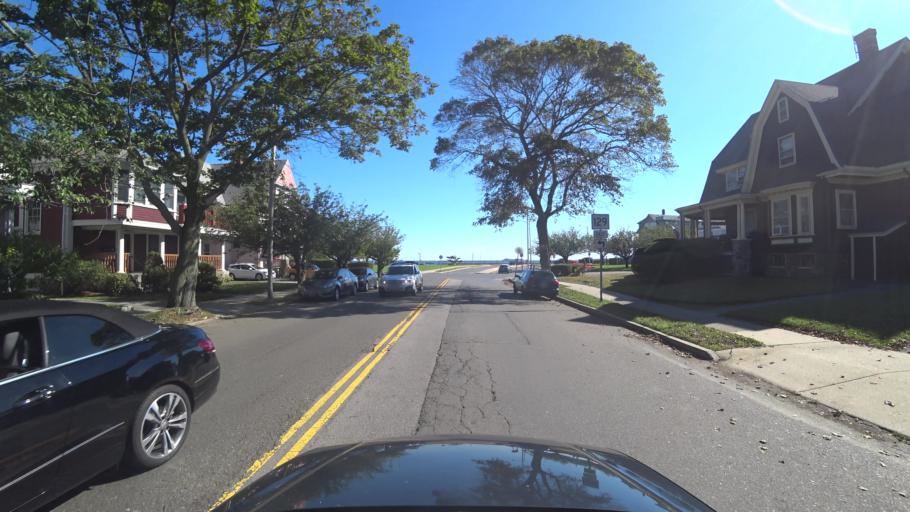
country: US
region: Massachusetts
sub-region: Essex County
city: Swampscott
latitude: 42.4679
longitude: -70.9227
